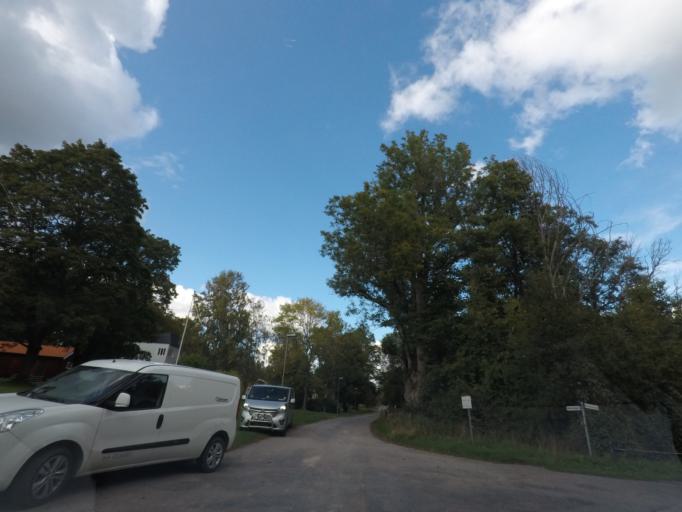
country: SE
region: Vaestmanland
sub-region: Skinnskattebergs Kommun
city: Skinnskatteberg
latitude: 59.8269
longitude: 15.6765
